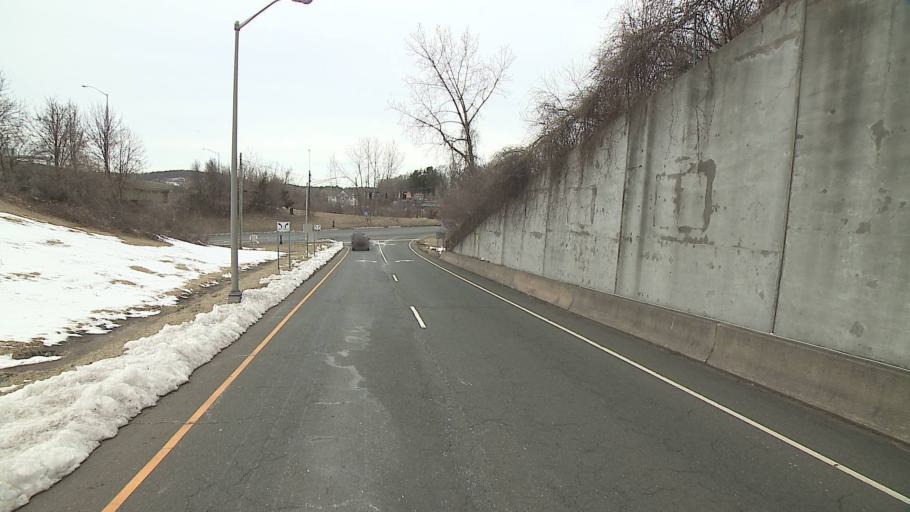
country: US
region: Connecticut
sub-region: Fairfield County
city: Danbury
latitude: 41.3802
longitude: -73.4738
